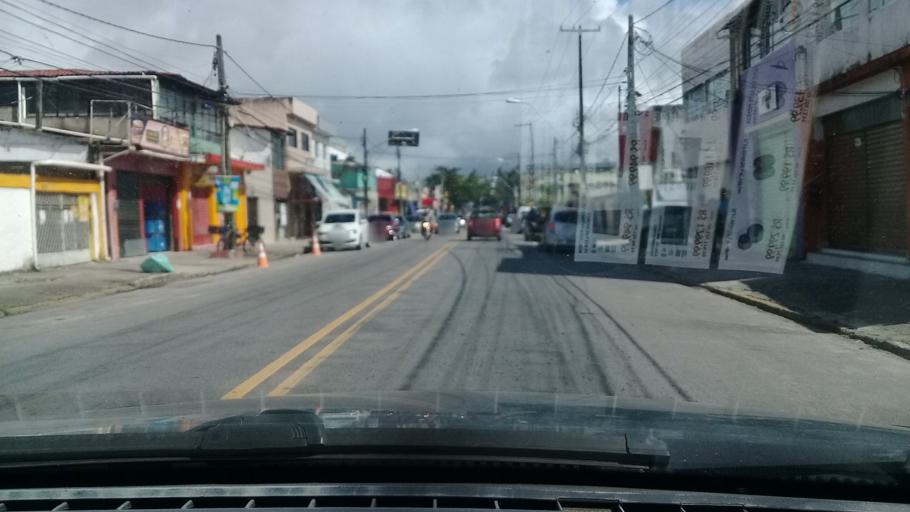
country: BR
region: Pernambuco
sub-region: Recife
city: Recife
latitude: -8.0682
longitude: -34.9281
